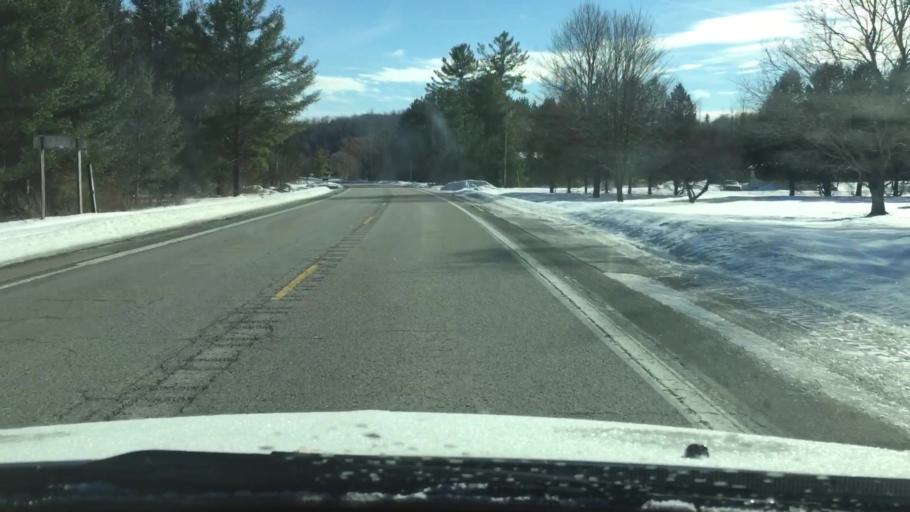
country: US
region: Michigan
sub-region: Charlevoix County
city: East Jordan
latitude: 45.1109
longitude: -85.1286
